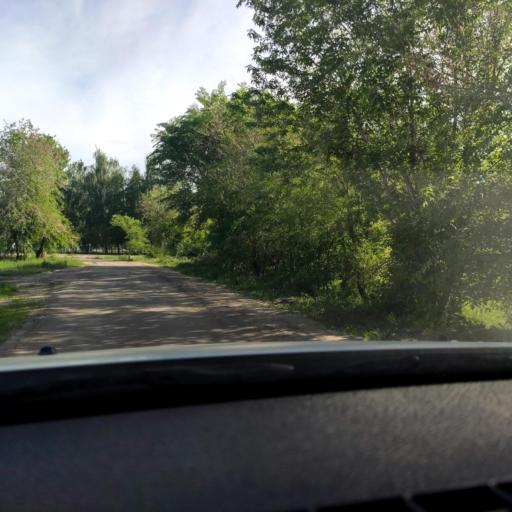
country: RU
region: Voronezj
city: Ramon'
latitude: 51.9392
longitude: 39.2051
